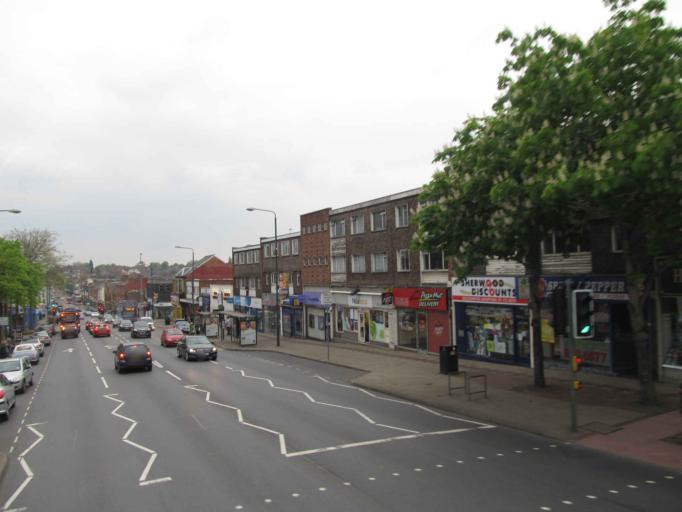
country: GB
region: England
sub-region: Nottinghamshire
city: Arnold
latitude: 52.9830
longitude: -1.1450
